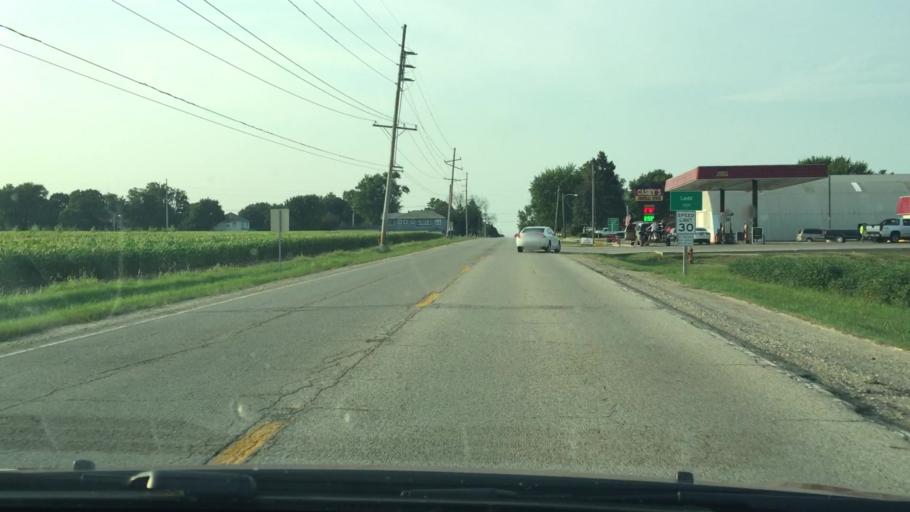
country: US
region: Illinois
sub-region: Bureau County
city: Ladd
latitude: 41.3767
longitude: -89.2190
